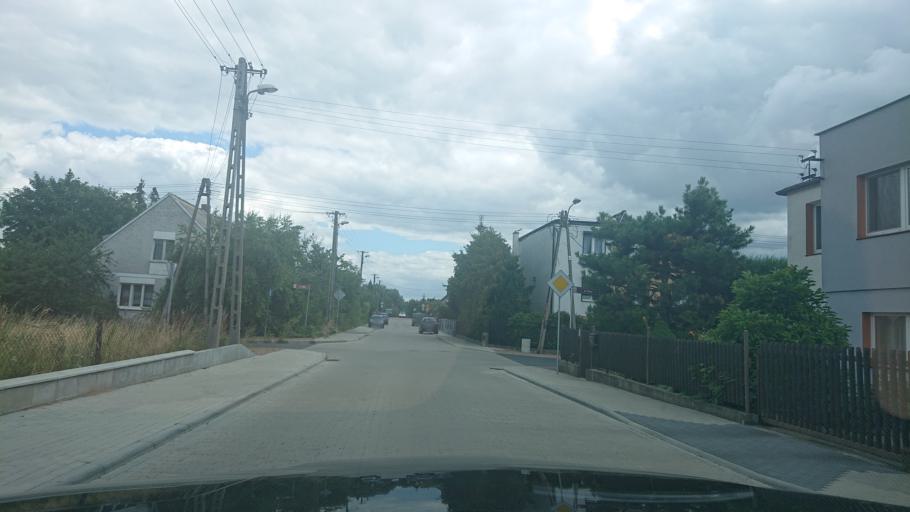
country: PL
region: Greater Poland Voivodeship
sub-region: Powiat gnieznienski
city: Gniezno
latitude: 52.5364
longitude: 17.6360
